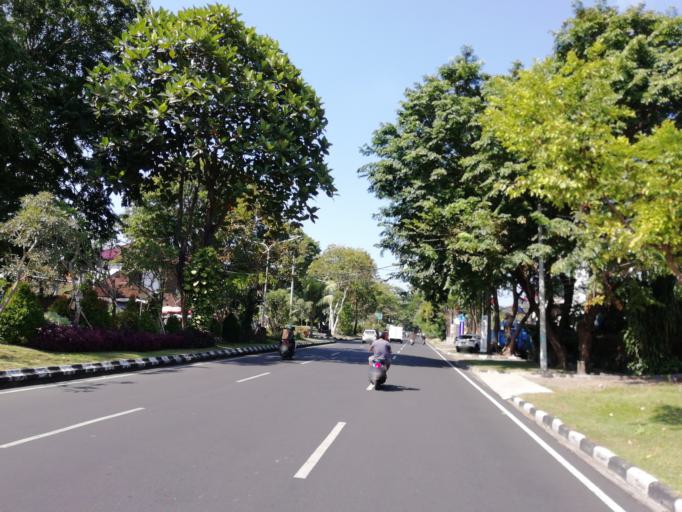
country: ID
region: Bali
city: Banjar Batanpoh
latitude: -8.6713
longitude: 115.2384
